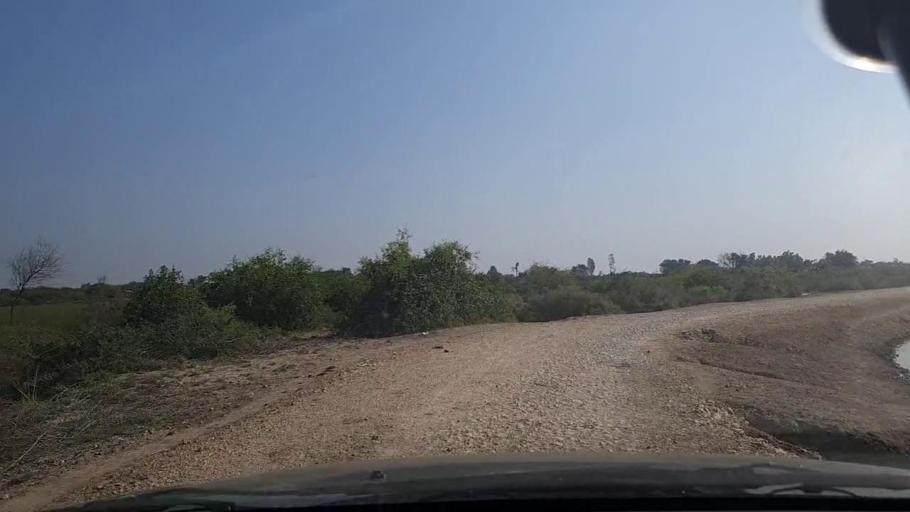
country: PK
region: Sindh
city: Chuhar Jamali
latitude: 24.5185
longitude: 67.8833
